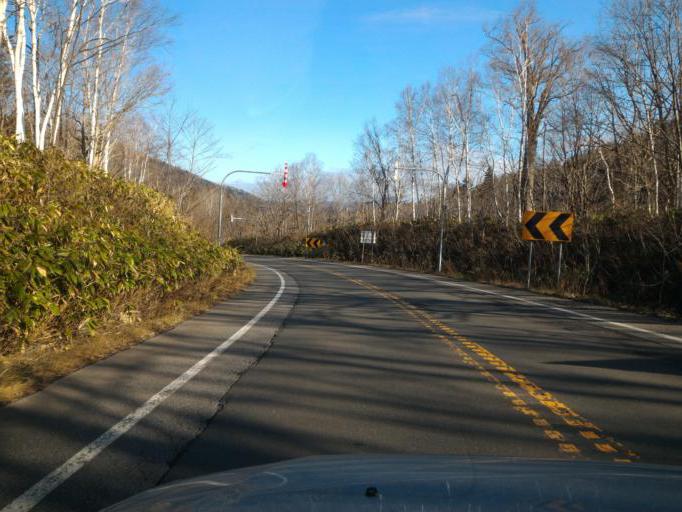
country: JP
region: Hokkaido
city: Ashibetsu
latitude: 43.2982
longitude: 142.1120
